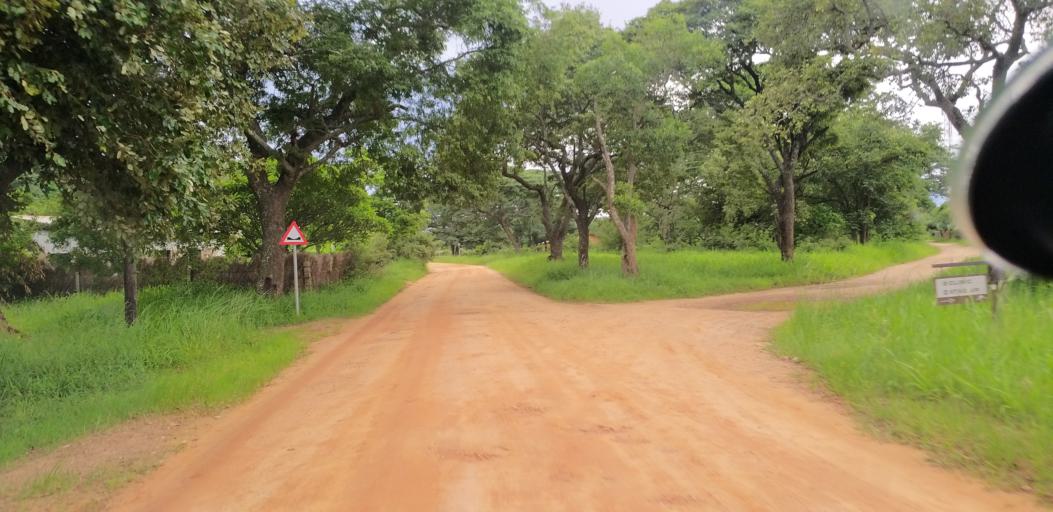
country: ZM
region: Lusaka
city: Chongwe
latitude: -15.1591
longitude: 28.4843
